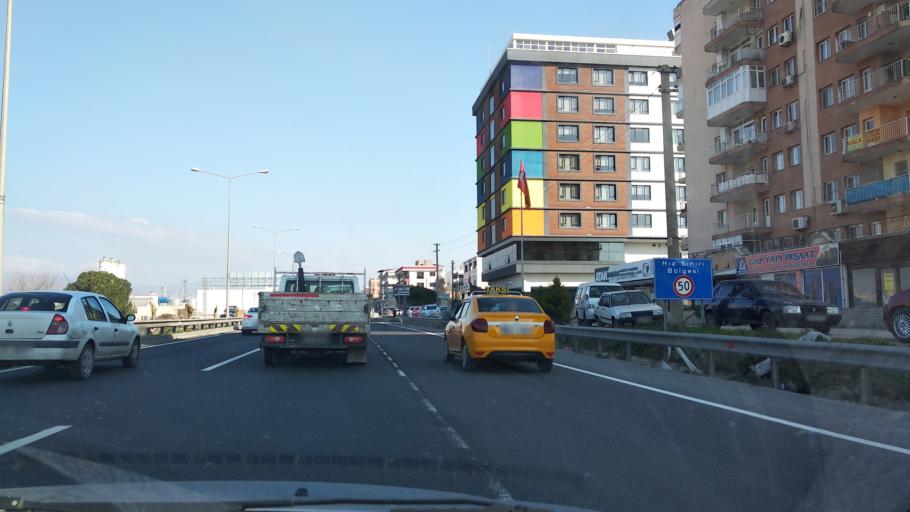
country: TR
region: Izmir
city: Menemen
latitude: 38.5723
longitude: 27.0589
